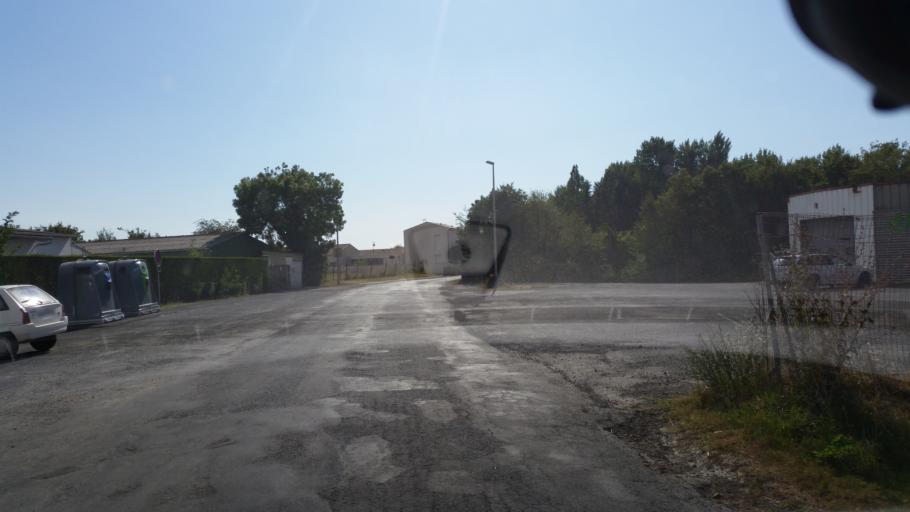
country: FR
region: Poitou-Charentes
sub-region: Departement de la Charente-Maritime
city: Marans
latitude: 46.3097
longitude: -1.0059
